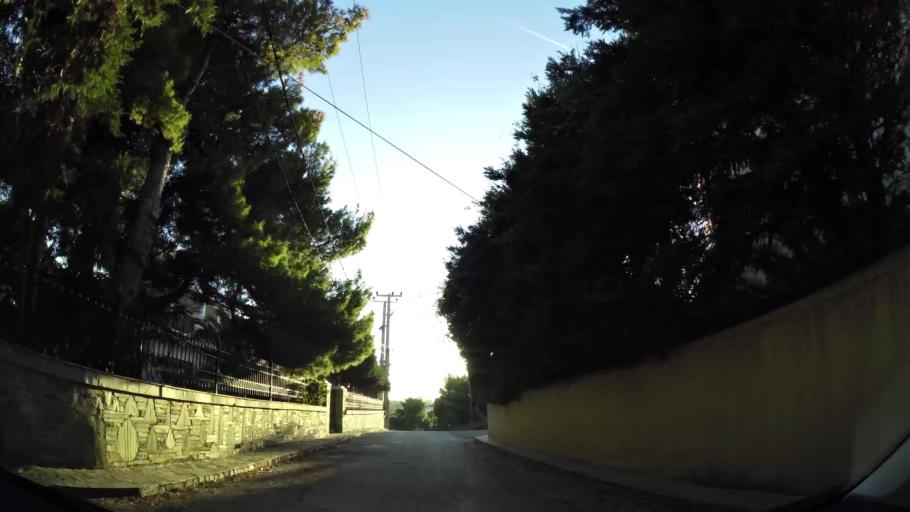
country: GR
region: Attica
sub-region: Nomarchia Anatolikis Attikis
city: Rafina
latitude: 38.0068
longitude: 24.0202
